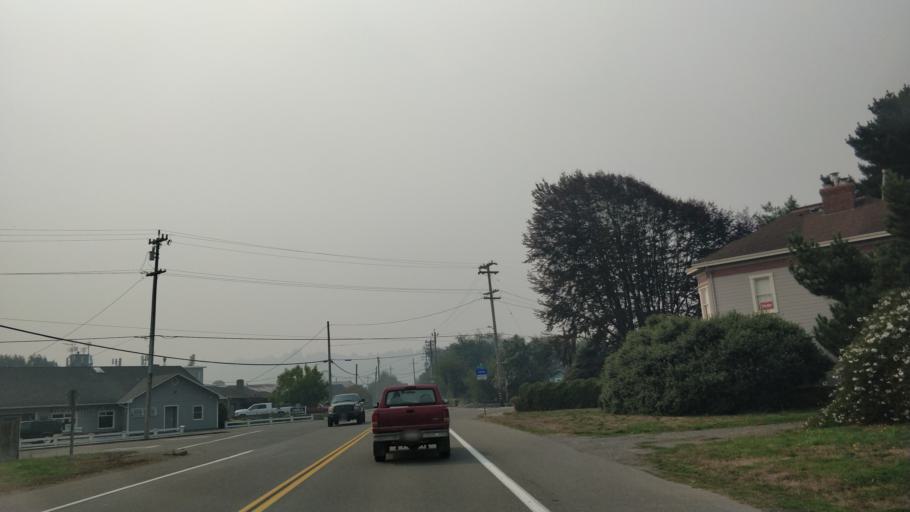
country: US
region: California
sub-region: Humboldt County
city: Ferndale
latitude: 40.5884
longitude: -124.2559
